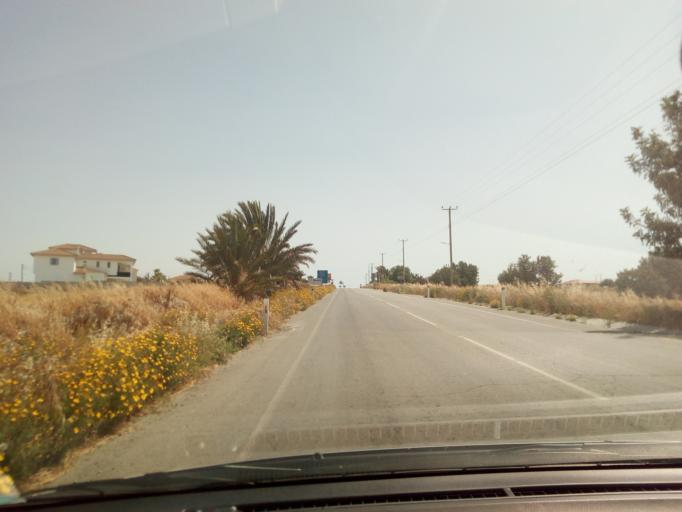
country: CY
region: Larnaka
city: Athienou
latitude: 35.0515
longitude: 33.5399
